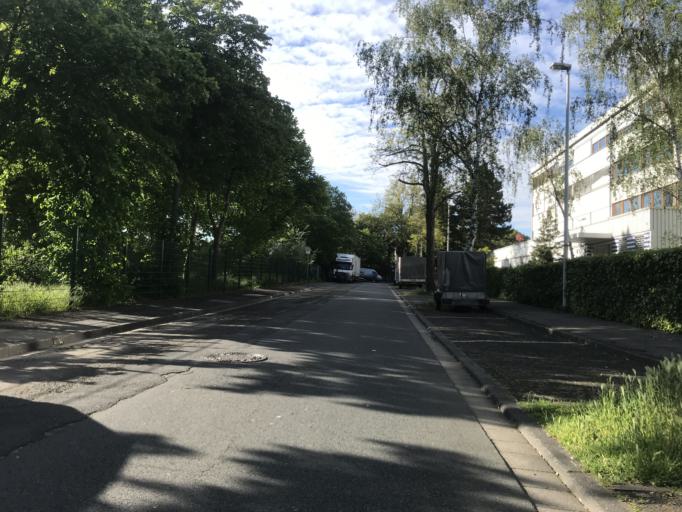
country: DE
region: Rheinland-Pfalz
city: Mainz
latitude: 50.0133
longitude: 8.2269
